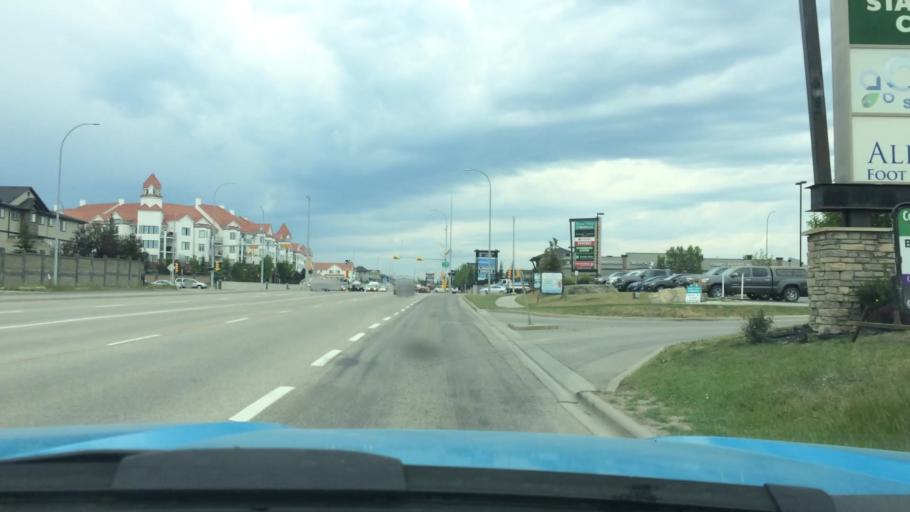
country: CA
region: Alberta
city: Calgary
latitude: 51.1489
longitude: -114.2121
